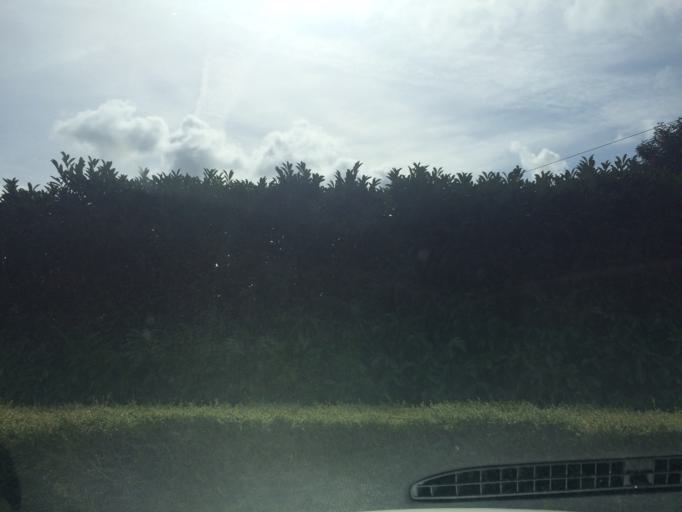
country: FR
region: Pays de la Loire
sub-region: Departement de la Loire-Atlantique
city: Arthon-en-Retz
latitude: 47.1168
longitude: -1.9321
